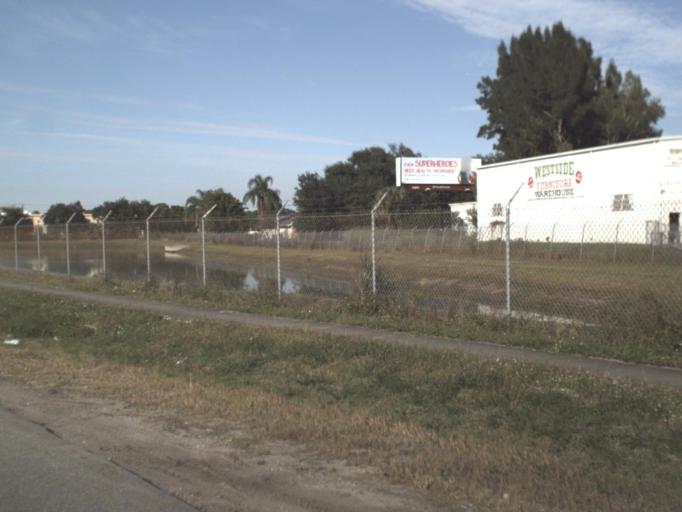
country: US
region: Florida
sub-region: Brevard County
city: June Park
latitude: 28.0758
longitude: -80.6720
